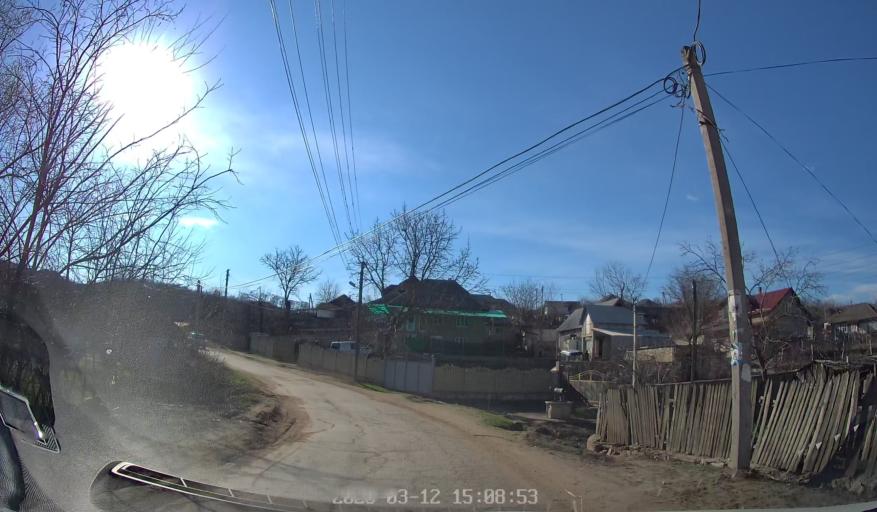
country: MD
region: Chisinau
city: Ciorescu
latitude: 47.2228
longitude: 28.9898
